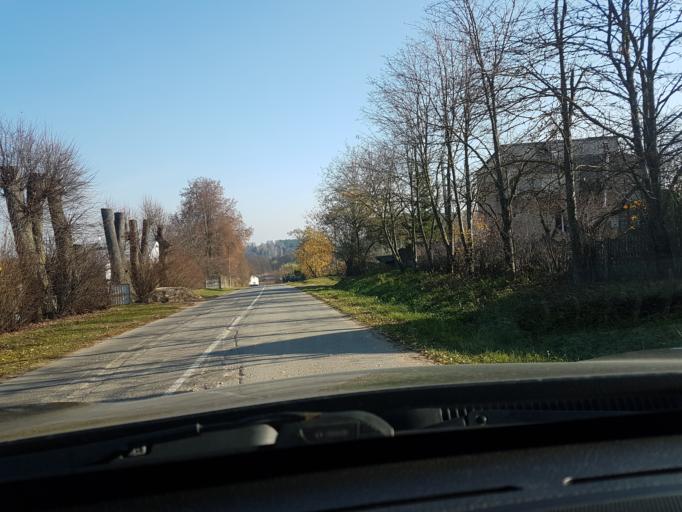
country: BY
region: Minsk
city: Azyartso
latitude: 53.8177
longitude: 27.3623
